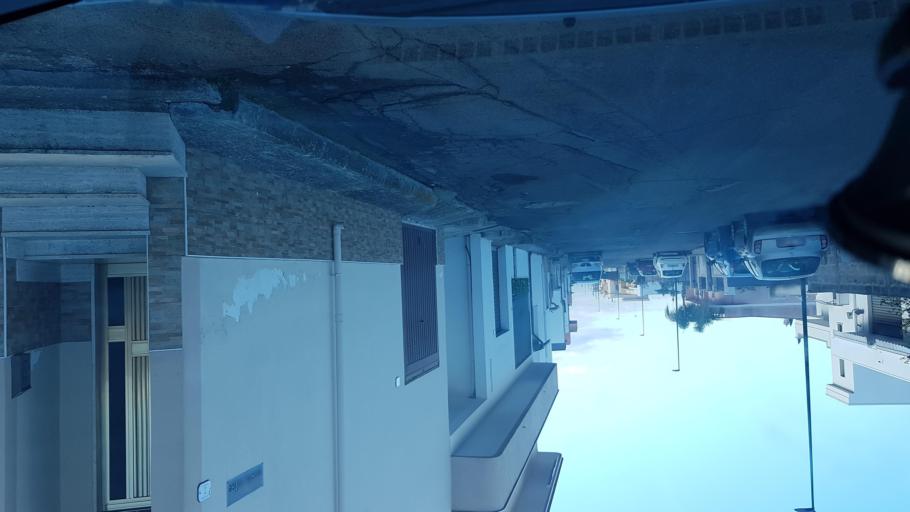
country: IT
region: Apulia
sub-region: Provincia di Lecce
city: Guagnano
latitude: 40.3994
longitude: 17.9534
